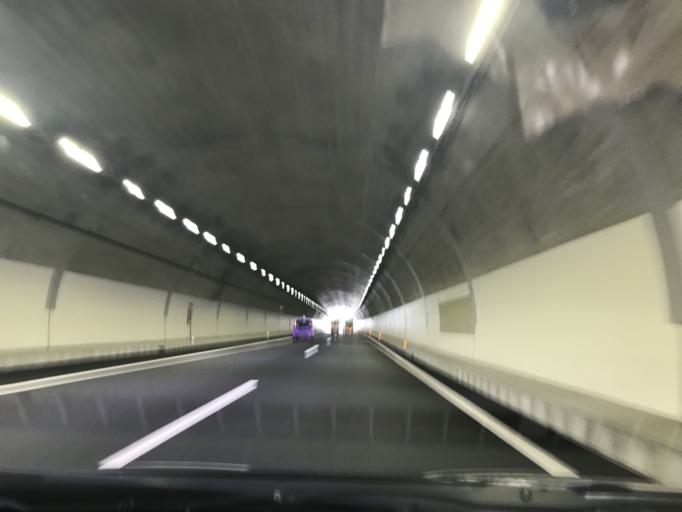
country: JP
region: Osaka
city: Takatsuki
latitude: 34.8944
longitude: 135.6077
